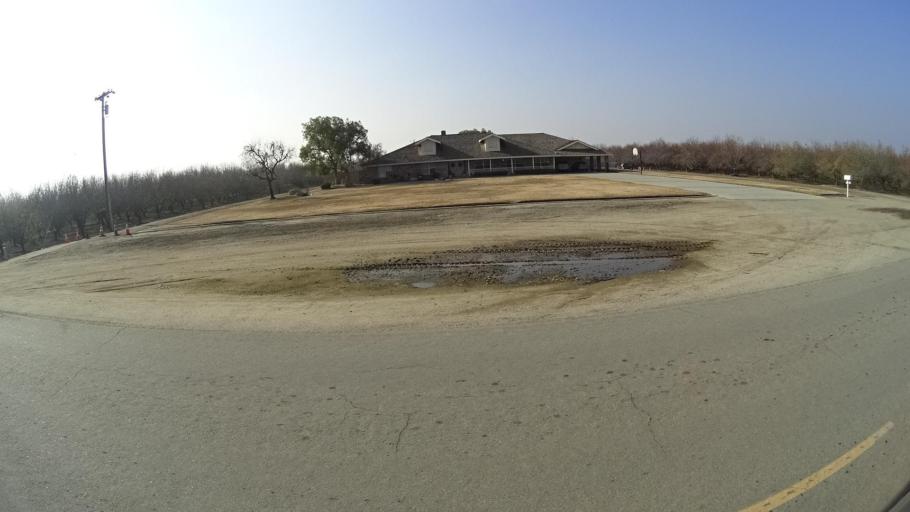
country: US
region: California
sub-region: Kern County
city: Greenfield
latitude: 35.2055
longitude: -119.0391
